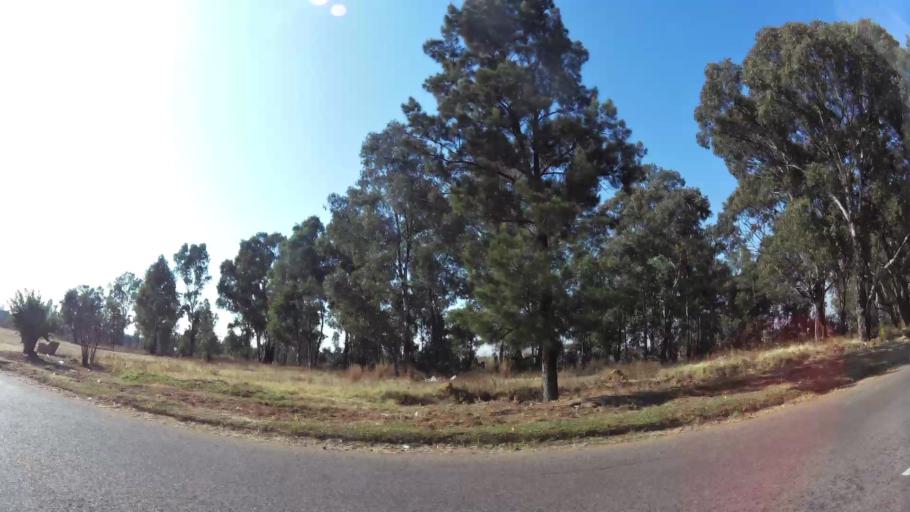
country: ZA
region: Gauteng
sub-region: Ekurhuleni Metropolitan Municipality
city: Boksburg
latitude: -26.2293
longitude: 28.2597
